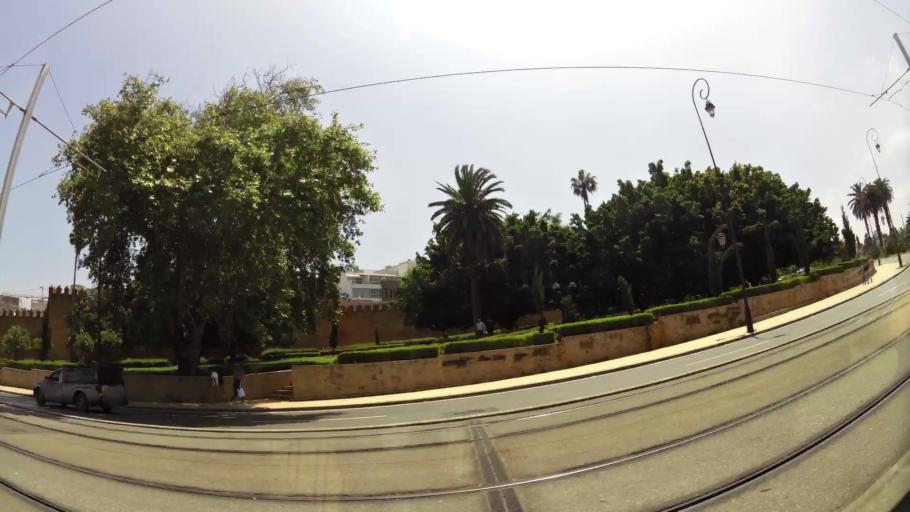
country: MA
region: Rabat-Sale-Zemmour-Zaer
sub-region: Rabat
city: Rabat
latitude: 34.0139
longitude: -6.8387
